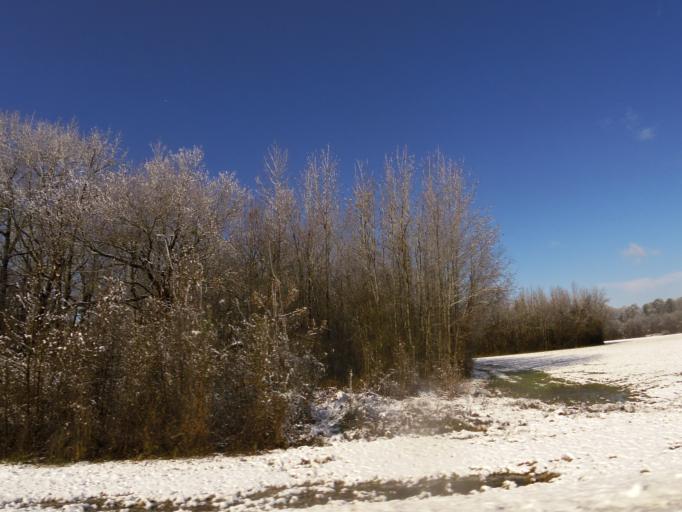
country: US
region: North Carolina
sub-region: Wilson County
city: Elm City
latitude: 35.7889
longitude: -77.8582
